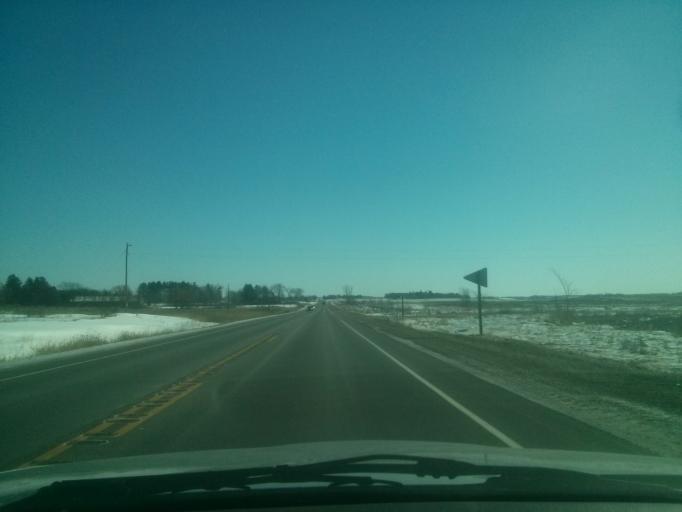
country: US
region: Wisconsin
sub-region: Polk County
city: Clear Lake
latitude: 45.1365
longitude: -92.3747
